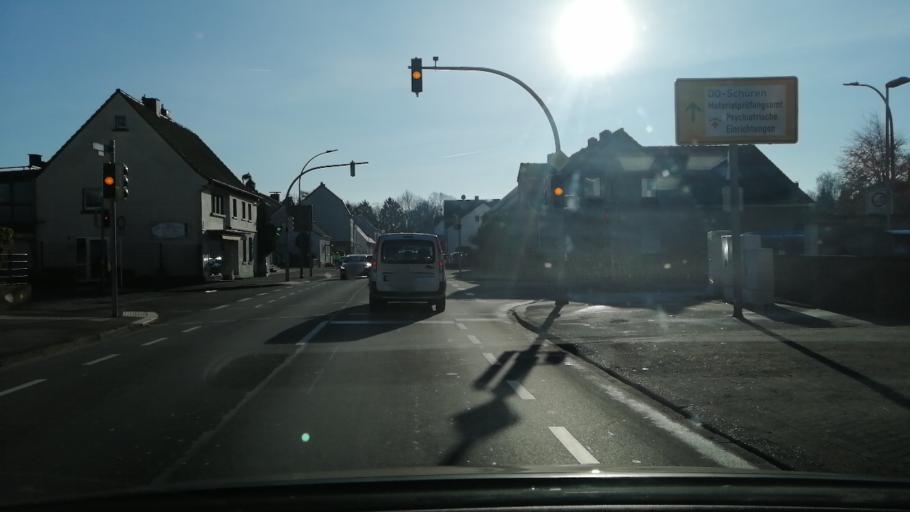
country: DE
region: North Rhine-Westphalia
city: Schwerte
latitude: 51.4994
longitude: 7.5607
